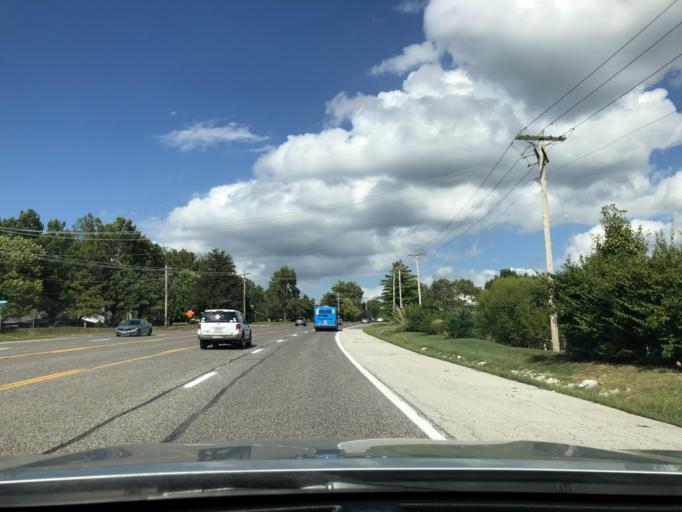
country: US
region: Missouri
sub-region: Saint Louis County
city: Lakeshire
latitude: 38.5357
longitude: -90.3382
